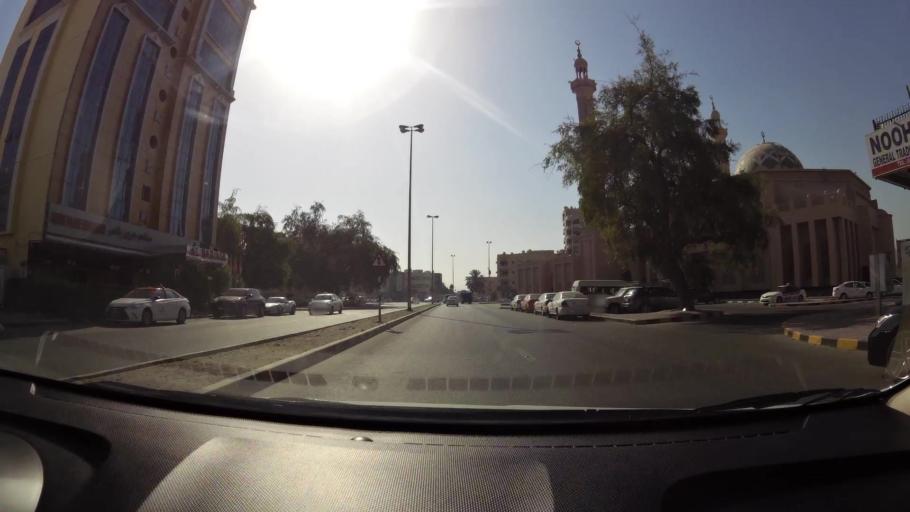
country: AE
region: Ajman
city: Ajman
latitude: 25.4149
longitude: 55.4455
